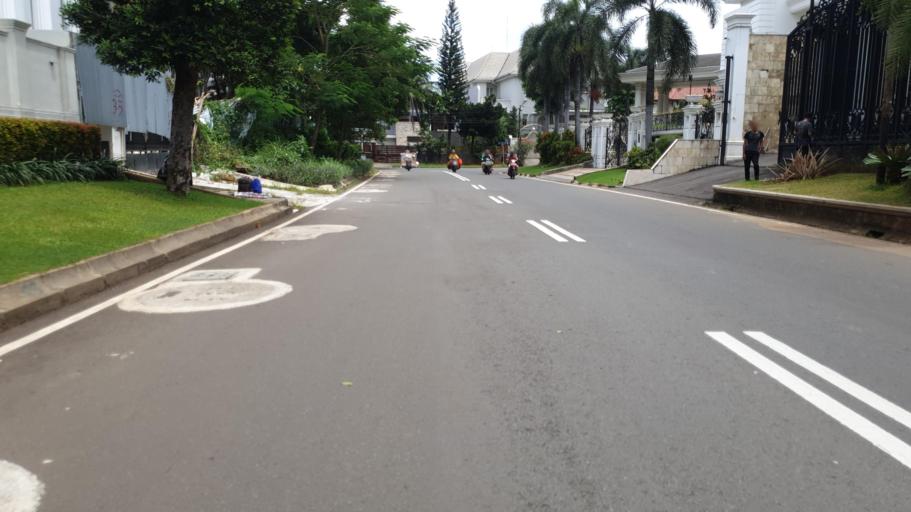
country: ID
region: Banten
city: South Tangerang
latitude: -6.2775
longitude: 106.7860
